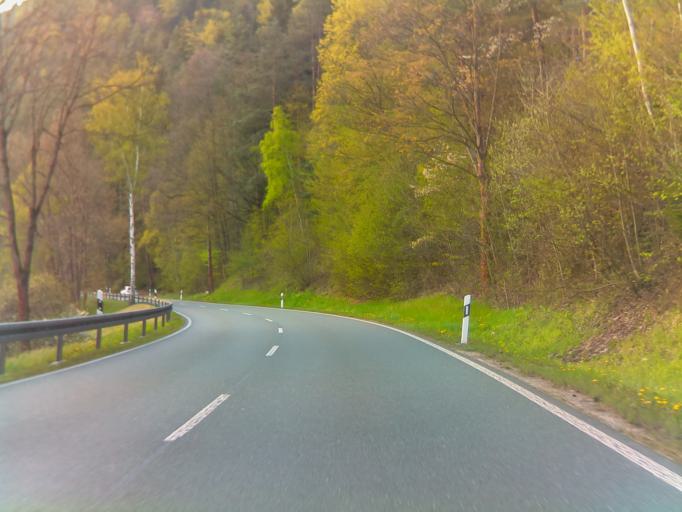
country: DE
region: Thuringia
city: Probstzella
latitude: 50.5434
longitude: 11.3682
